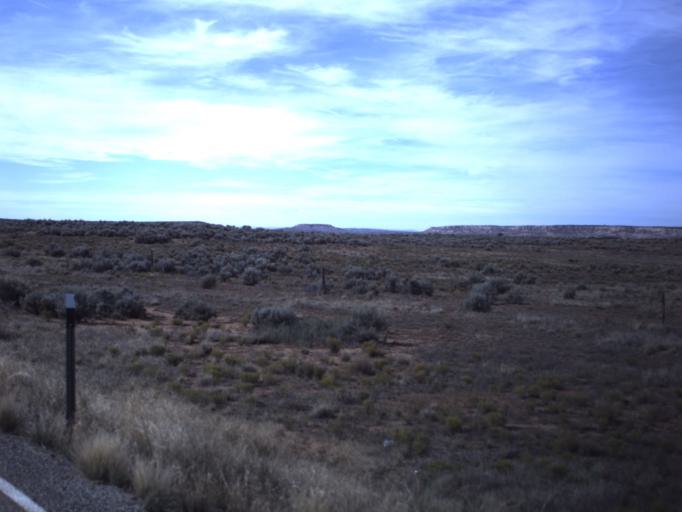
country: US
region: Utah
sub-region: San Juan County
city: Blanding
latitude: 37.3850
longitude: -109.3406
